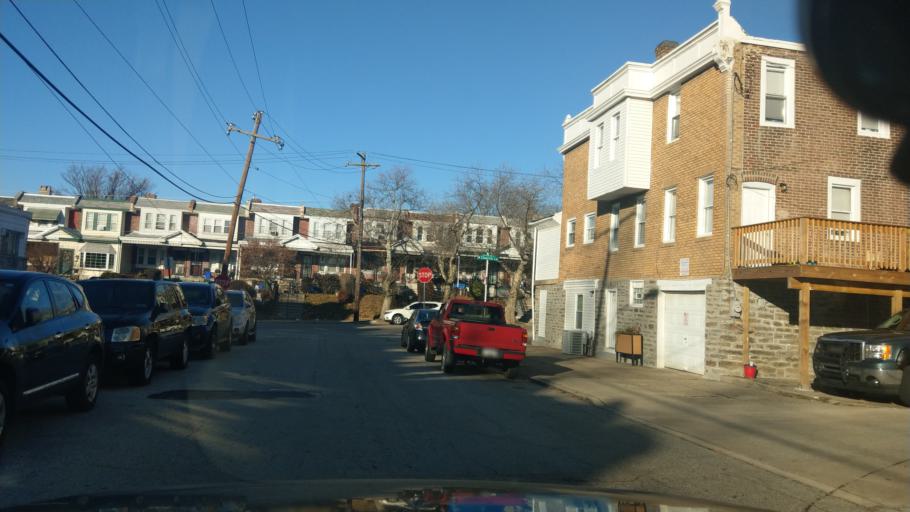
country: US
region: Pennsylvania
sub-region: Montgomery County
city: Wyncote
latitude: 40.0460
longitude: -75.1519
